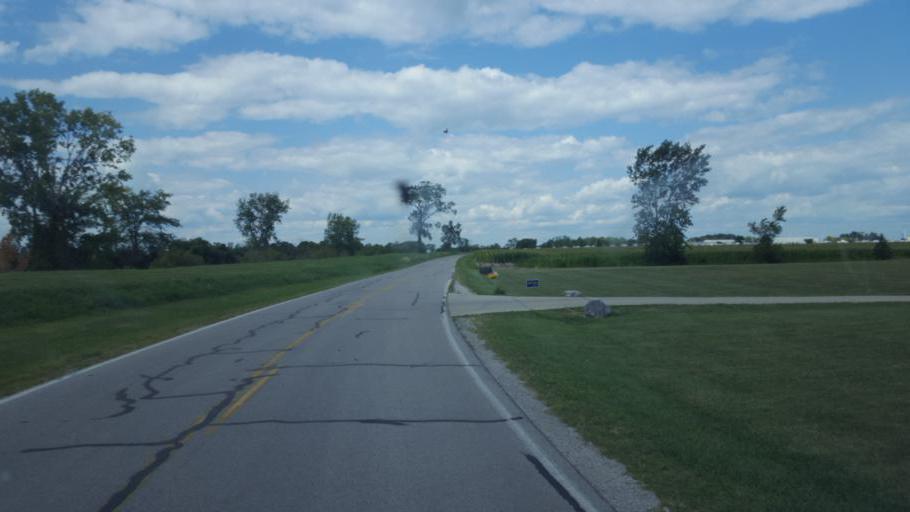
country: US
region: Ohio
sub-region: Lucas County
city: Curtice
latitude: 41.6618
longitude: -83.2928
